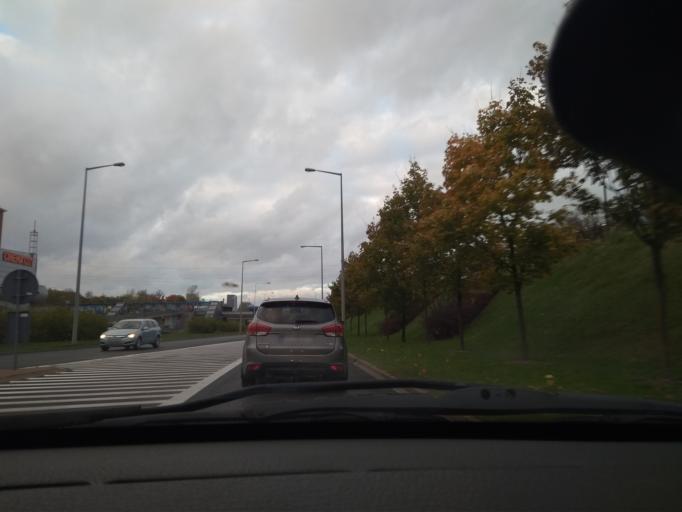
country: PL
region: Greater Poland Voivodeship
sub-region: Poznan
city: Poznan
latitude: 52.4406
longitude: 16.9207
